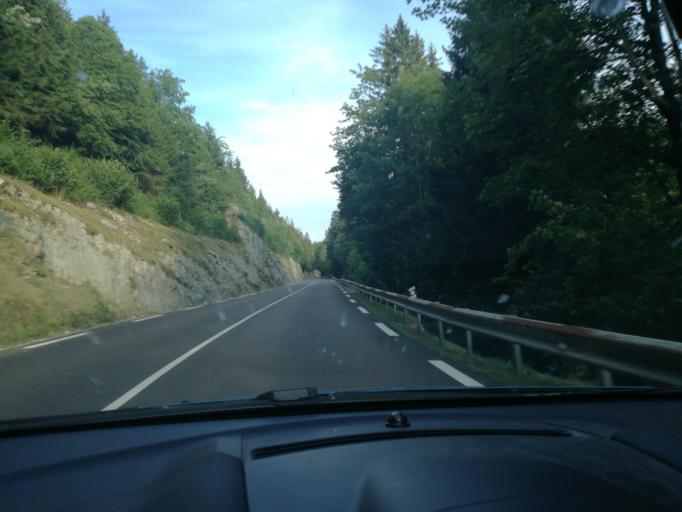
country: FR
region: Franche-Comte
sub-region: Departement du Jura
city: Morbier
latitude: 46.6260
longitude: 5.9545
